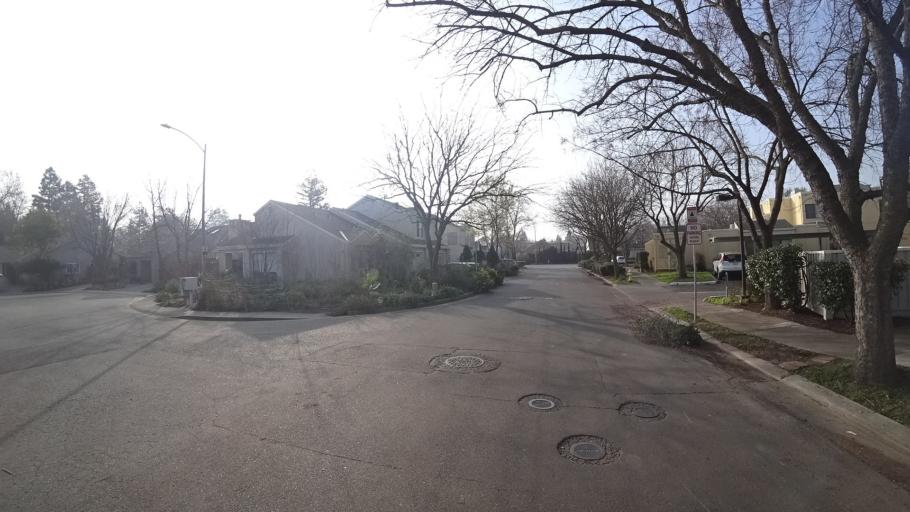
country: US
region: California
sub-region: Yolo County
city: Davis
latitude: 38.5651
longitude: -121.7641
